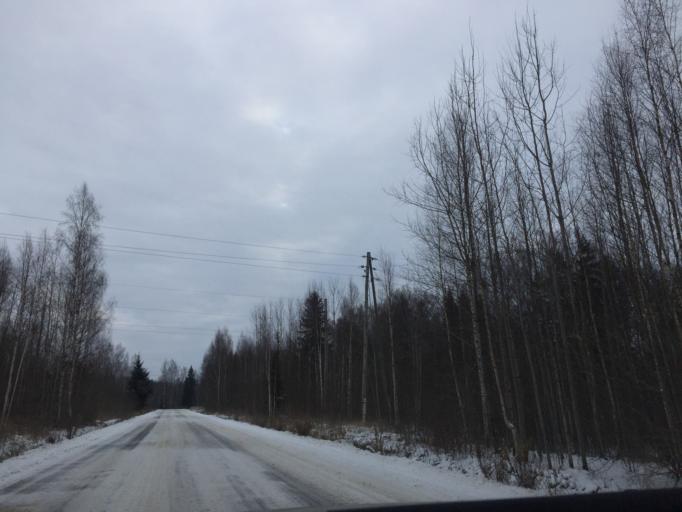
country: LV
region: Amatas Novads
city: Drabesi
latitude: 57.2139
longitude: 25.1701
